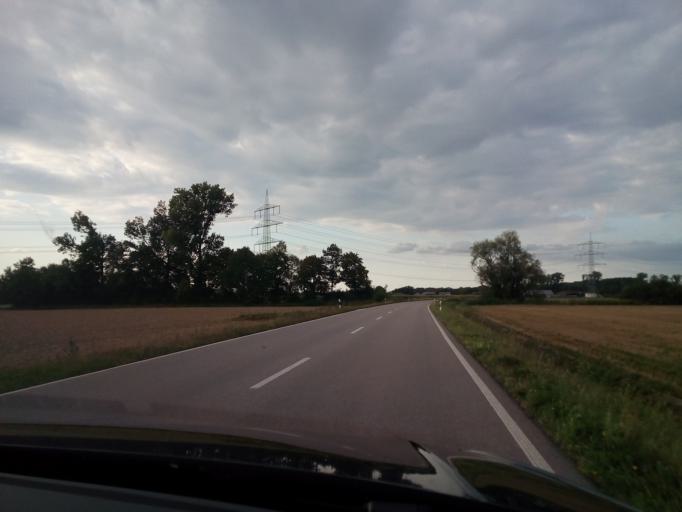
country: DE
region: Baden-Wuerttemberg
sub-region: Freiburg Region
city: Rheinau
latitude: 48.6623
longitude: 7.9932
